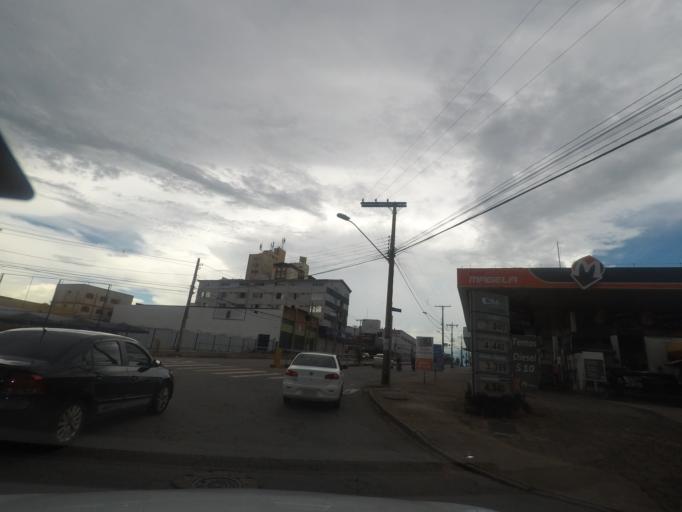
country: BR
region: Goias
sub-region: Goiania
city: Goiania
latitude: -16.6719
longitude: -49.2475
